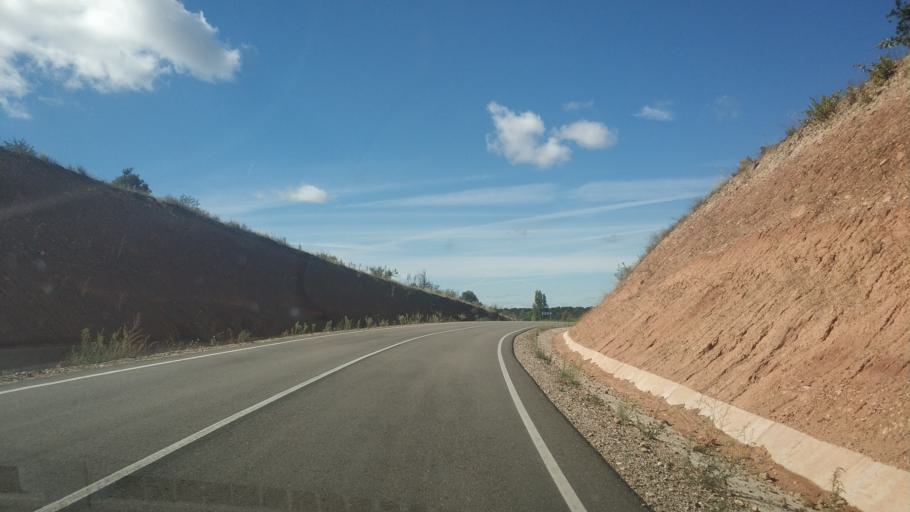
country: ES
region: Castille and Leon
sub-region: Provincia de Burgos
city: Covarrubias
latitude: 42.0463
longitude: -3.5453
